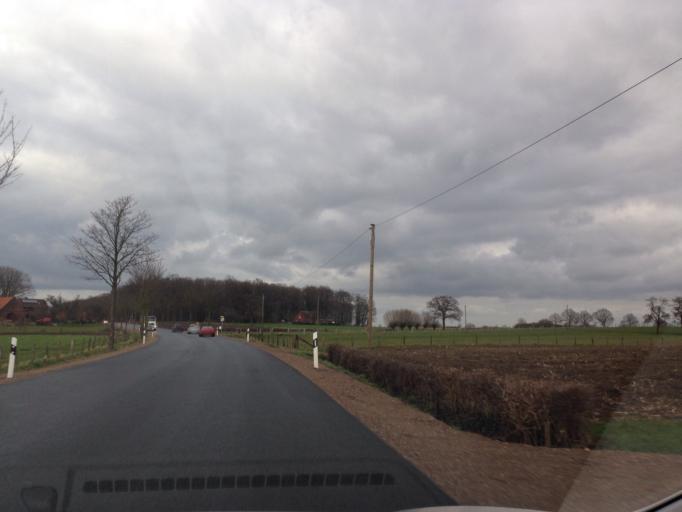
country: DE
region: North Rhine-Westphalia
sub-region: Regierungsbezirk Munster
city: Nordkirchen
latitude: 51.7717
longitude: 7.5444
